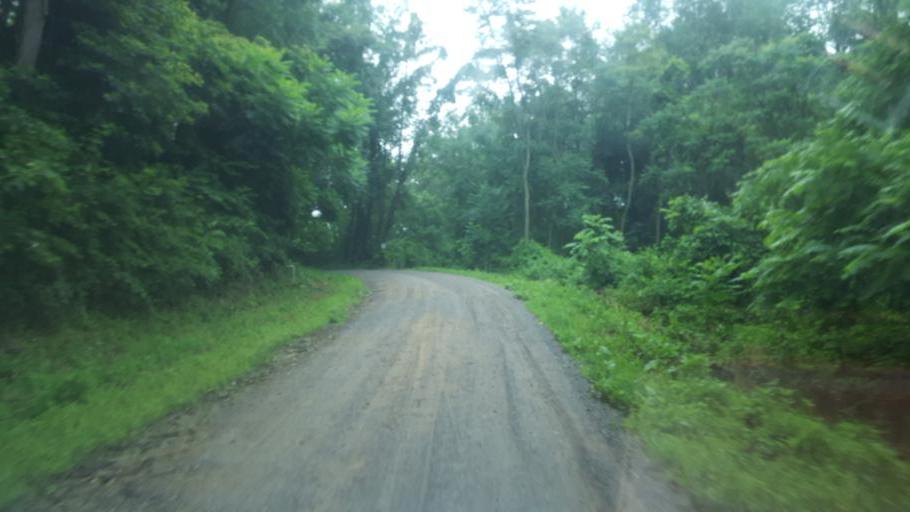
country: US
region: Ohio
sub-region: Columbiana County
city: Salineville
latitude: 40.5459
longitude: -80.8304
